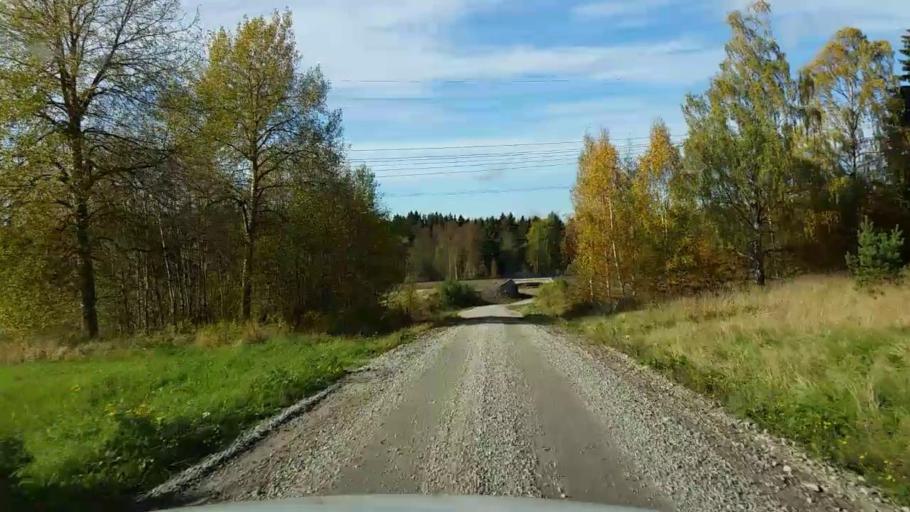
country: SE
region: Gaevleborg
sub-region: Ljusdals Kommun
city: Jaervsoe
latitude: 61.7842
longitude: 16.1617
